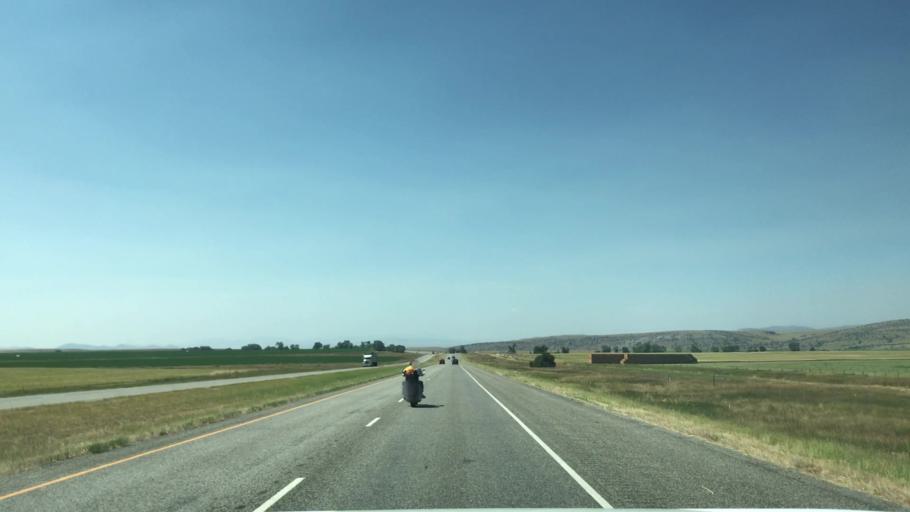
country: US
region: Montana
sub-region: Gallatin County
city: Manhattan
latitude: 45.8658
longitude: -111.3695
